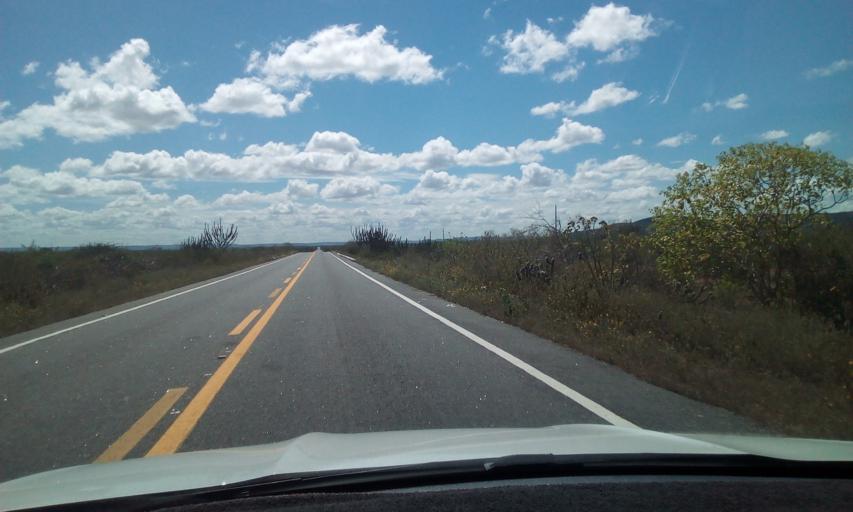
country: BR
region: Paraiba
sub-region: Areia
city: Remigio
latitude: -6.8725
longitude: -35.9239
